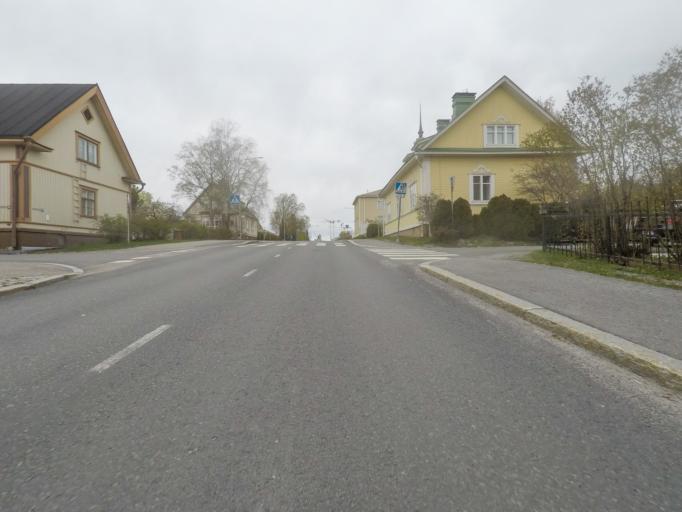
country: FI
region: Pirkanmaa
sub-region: Tampere
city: Tampere
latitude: 61.4853
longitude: 23.7861
